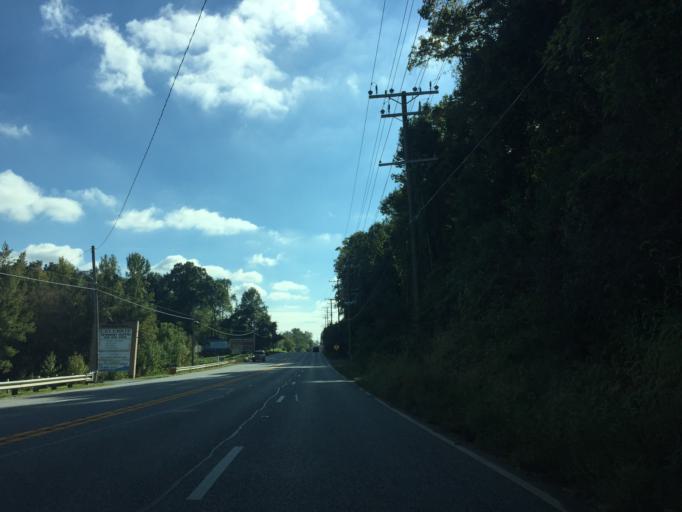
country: US
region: Maryland
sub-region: Baltimore County
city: Kingsville
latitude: 39.4597
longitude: -76.4138
